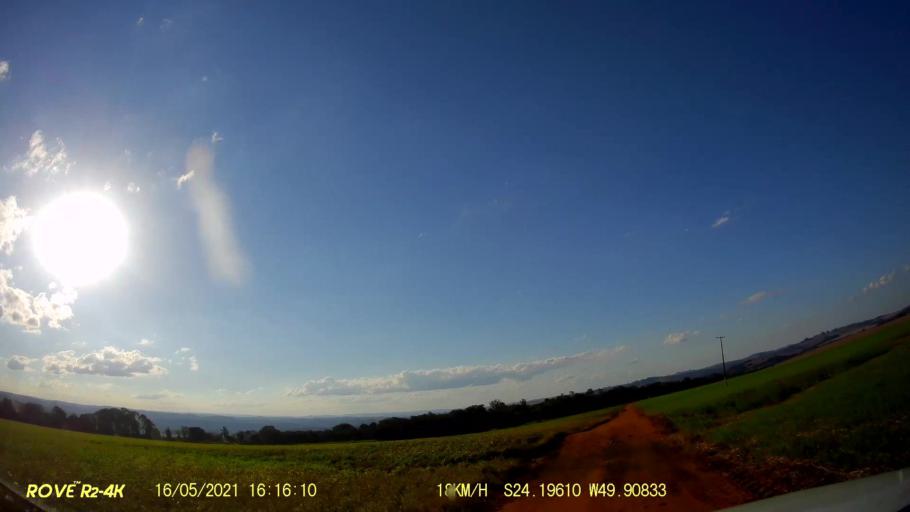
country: BR
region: Parana
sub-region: Jaguariaiva
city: Jaguariaiva
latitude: -24.1948
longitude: -49.9073
